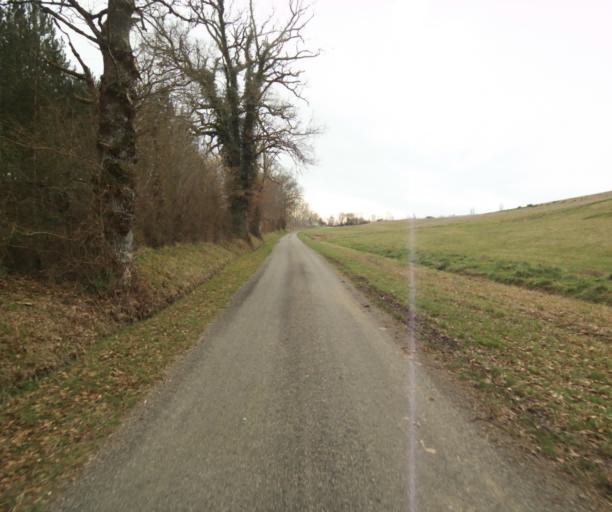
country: FR
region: Midi-Pyrenees
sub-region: Departement du Gers
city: Eauze
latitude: 43.9157
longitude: 0.0612
